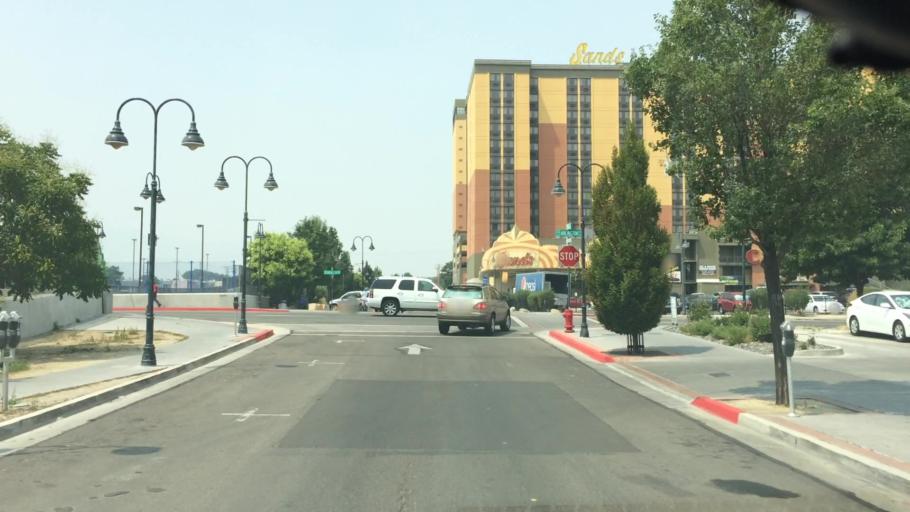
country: US
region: Nevada
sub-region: Washoe County
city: Reno
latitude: 39.5280
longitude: -119.8173
